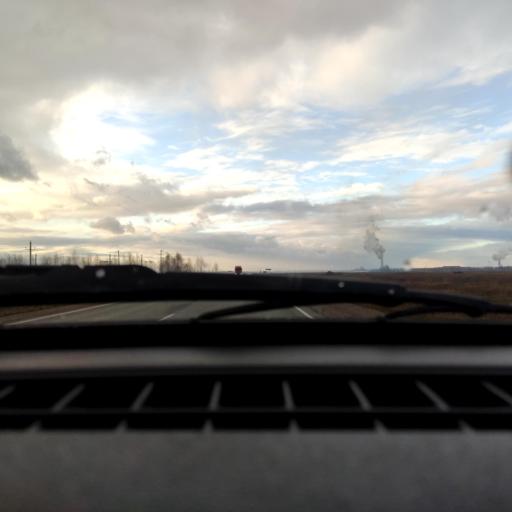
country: RU
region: Bashkortostan
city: Iglino
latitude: 54.7512
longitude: 56.2896
